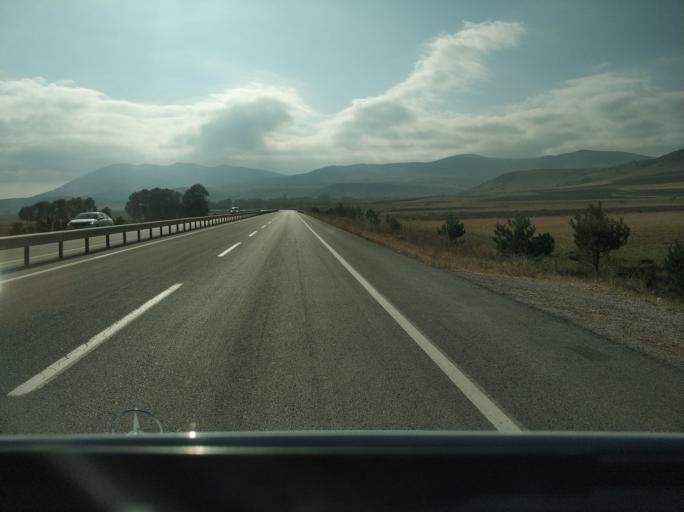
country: TR
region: Sivas
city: Yildizeli
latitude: 39.8495
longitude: 36.5129
